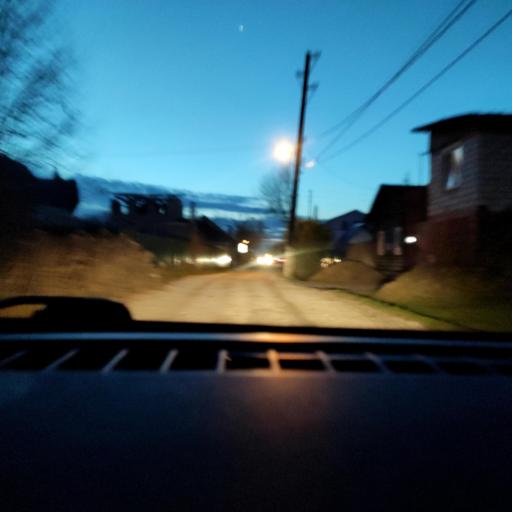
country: RU
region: Perm
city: Perm
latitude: 58.0501
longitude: 56.3325
